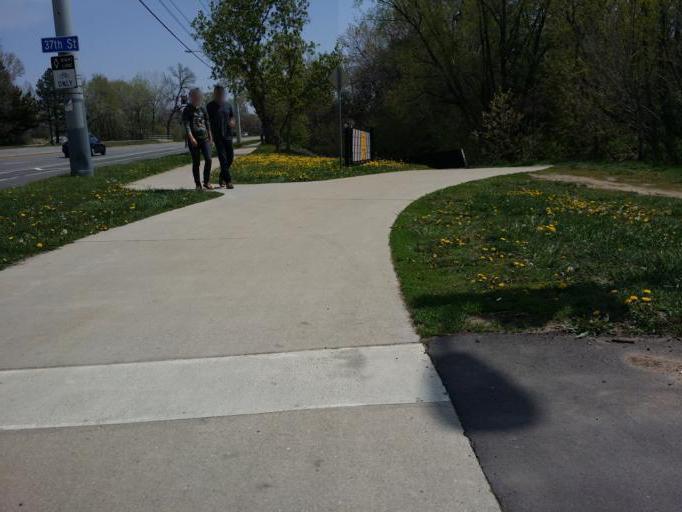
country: US
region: Colorado
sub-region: Boulder County
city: Boulder
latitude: 39.9999
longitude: -105.2465
